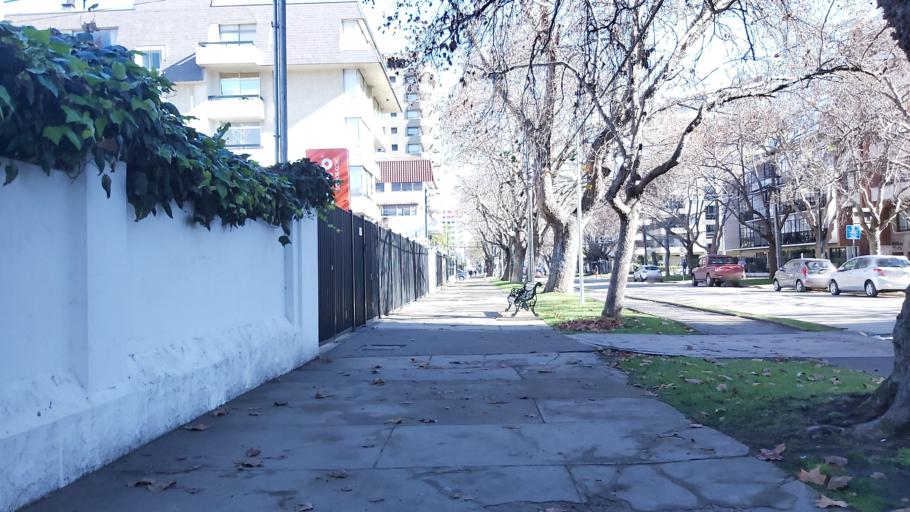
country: CL
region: Valparaiso
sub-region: Provincia de Valparaiso
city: Vina del Mar
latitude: -33.0158
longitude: -71.5477
